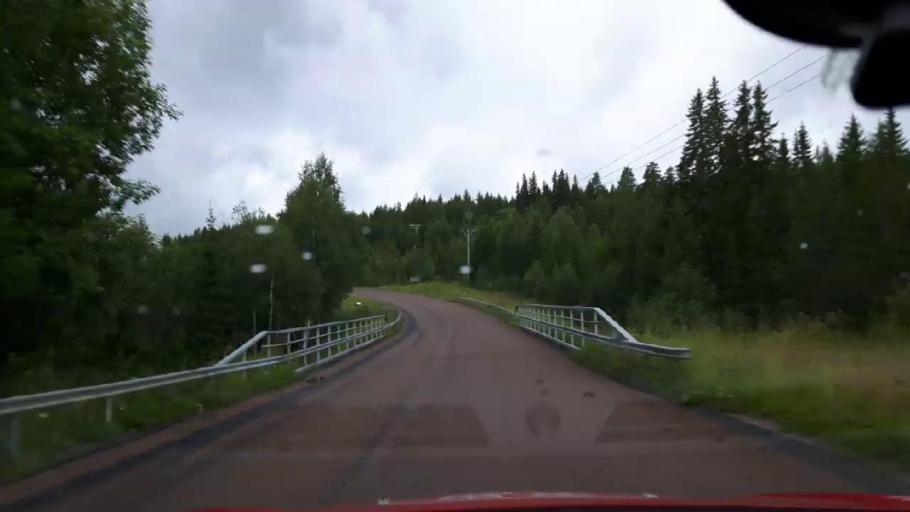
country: SE
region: Jaemtland
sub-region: Are Kommun
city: Jarpen
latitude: 63.3286
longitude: 13.6942
